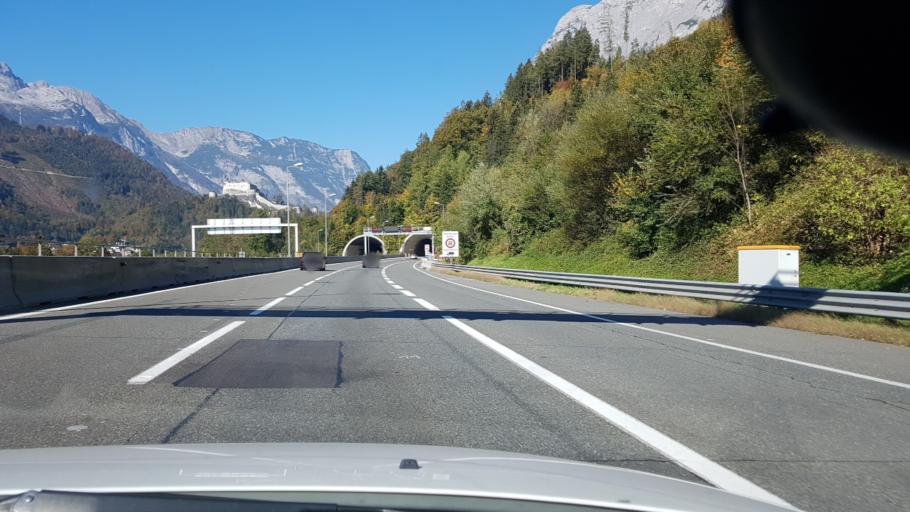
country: AT
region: Salzburg
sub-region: Politischer Bezirk Sankt Johann im Pongau
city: Pfarrwerfen
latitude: 47.4707
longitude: 13.1992
